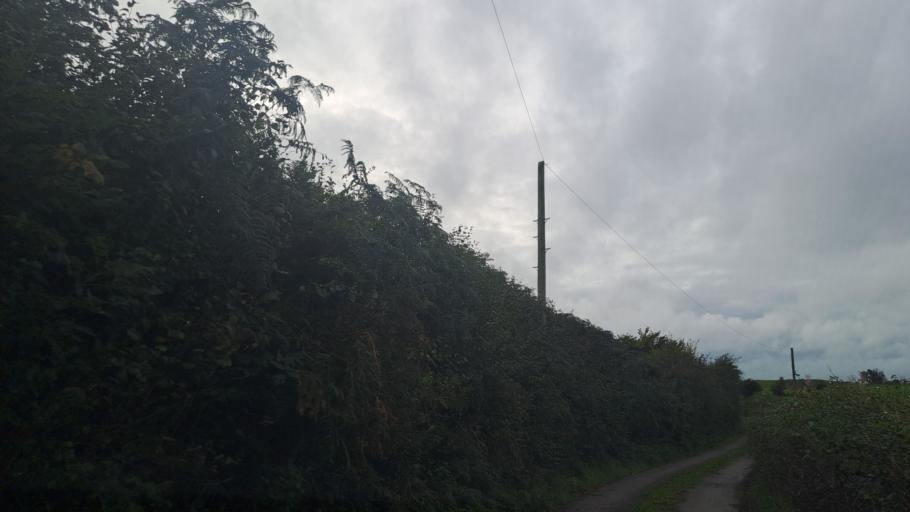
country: IE
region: Ulster
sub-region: An Cabhan
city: Bailieborough
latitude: 53.9827
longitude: -6.8954
